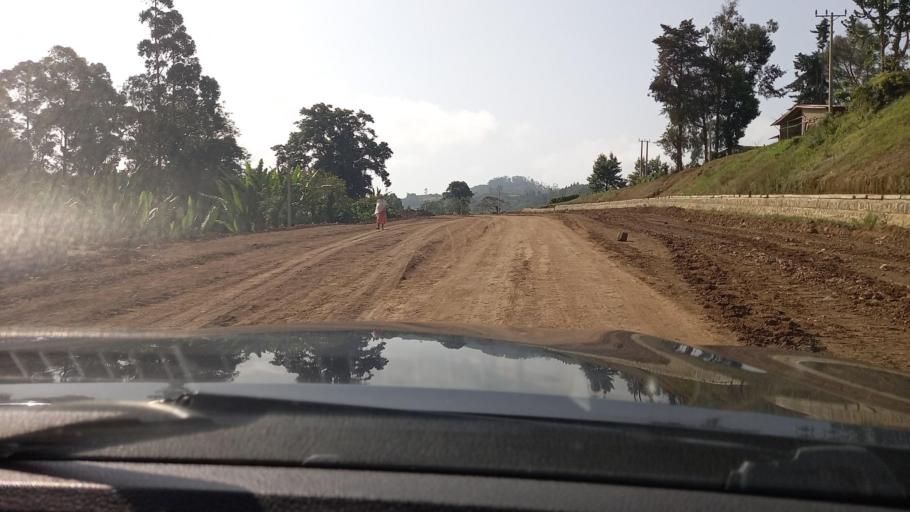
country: ET
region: Southern Nations, Nationalities, and People's Region
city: Mizan Teferi
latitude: 6.1669
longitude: 35.5855
